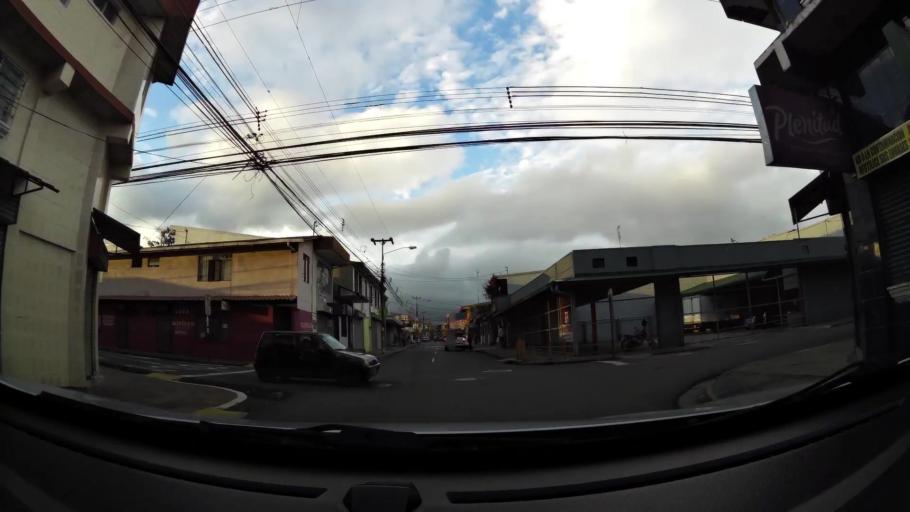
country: CR
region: Heredia
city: Heredia
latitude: 9.9938
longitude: -84.1175
